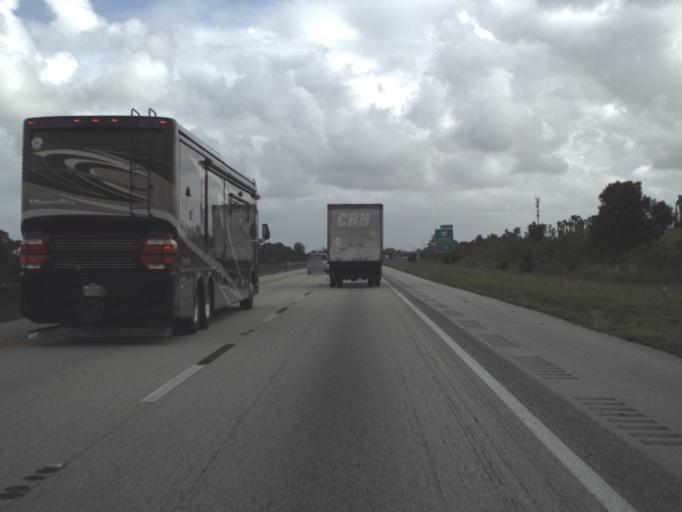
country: US
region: Florida
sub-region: Palm Beach County
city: Limestone Creek
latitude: 26.9486
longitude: -80.1615
